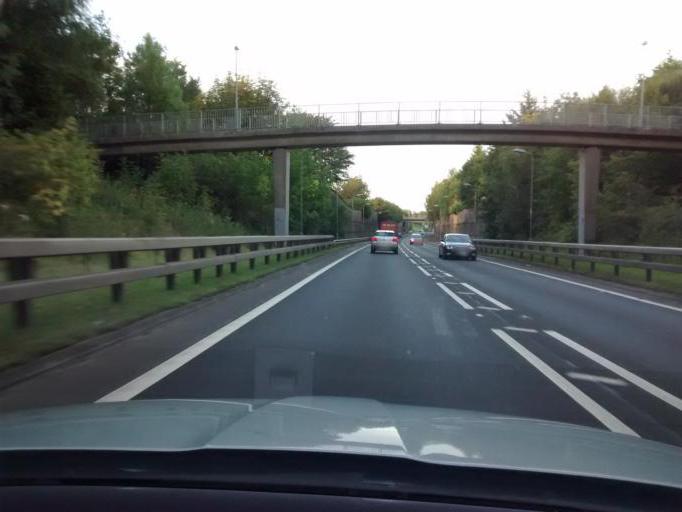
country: GB
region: Scotland
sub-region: Renfrewshire
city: Kilbarchan
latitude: 55.8283
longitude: -4.5382
